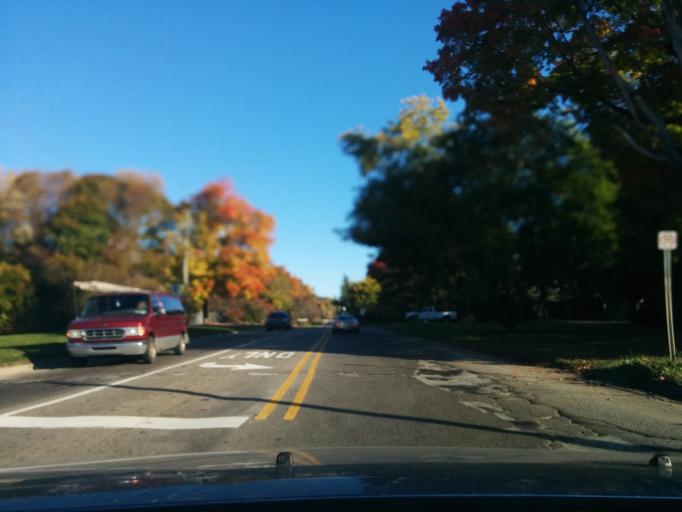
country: US
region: Michigan
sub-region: Wayne County
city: Northville
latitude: 42.4232
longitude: -83.5118
